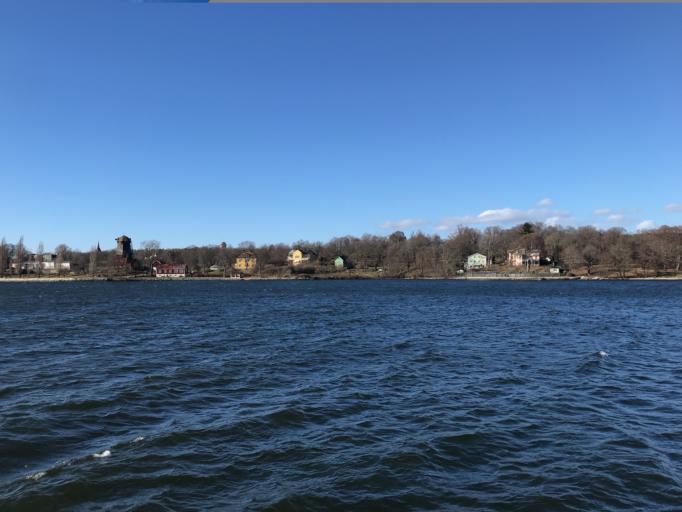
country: SE
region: Stockholm
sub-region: Stockholms Kommun
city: OEstermalm
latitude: 59.3173
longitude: 18.1209
